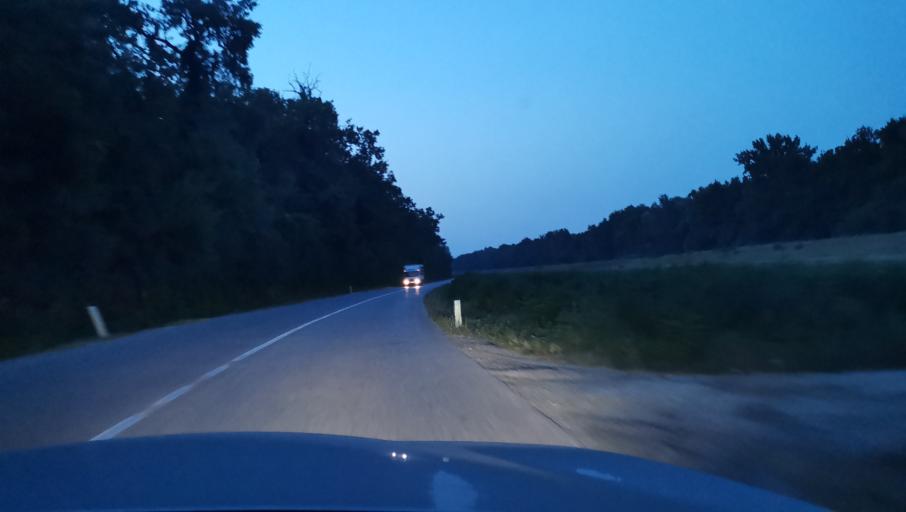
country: RS
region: Central Serbia
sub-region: Belgrade
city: Obrenovac
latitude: 44.6900
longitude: 20.1963
